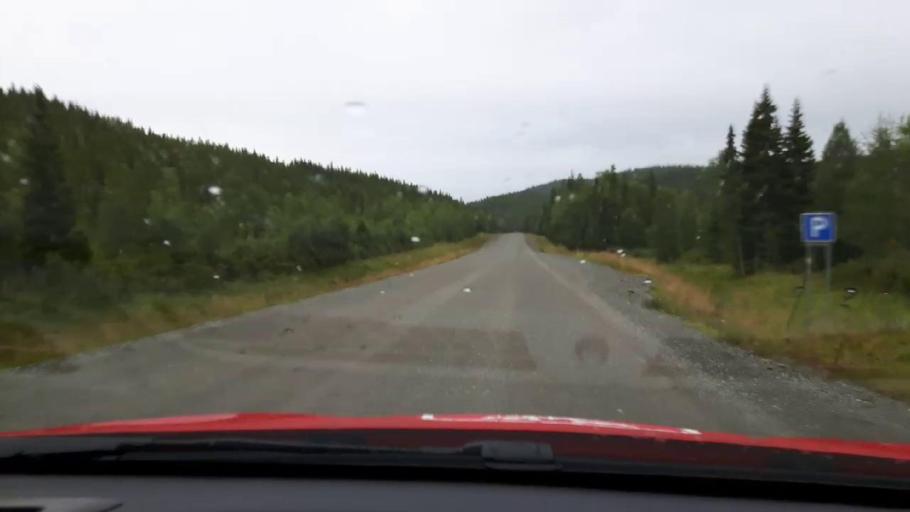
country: SE
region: Jaemtland
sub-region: Are Kommun
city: Are
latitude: 63.4287
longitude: 12.7376
